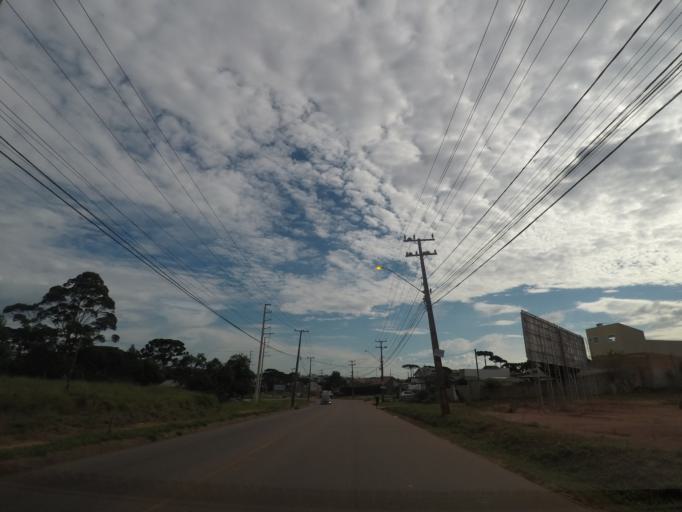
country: BR
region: Parana
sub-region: Araucaria
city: Araucaria
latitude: -25.6361
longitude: -49.2968
